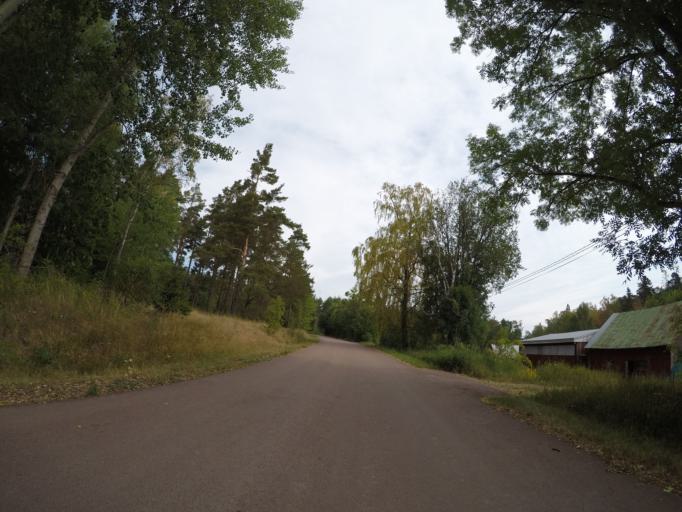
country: AX
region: Alands landsbygd
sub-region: Finstroem
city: Finstroem
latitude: 60.2536
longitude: 19.9143
